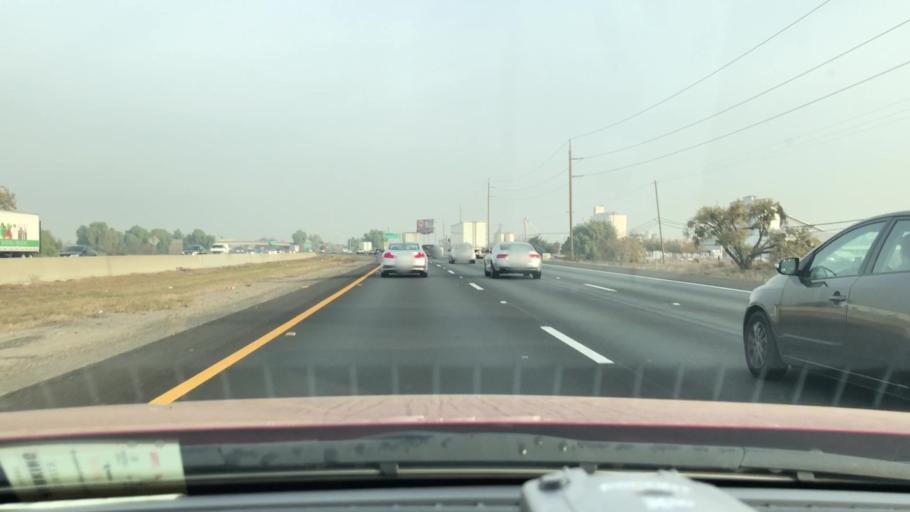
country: US
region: California
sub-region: San Joaquin County
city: French Camp
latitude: 37.8693
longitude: -121.2782
